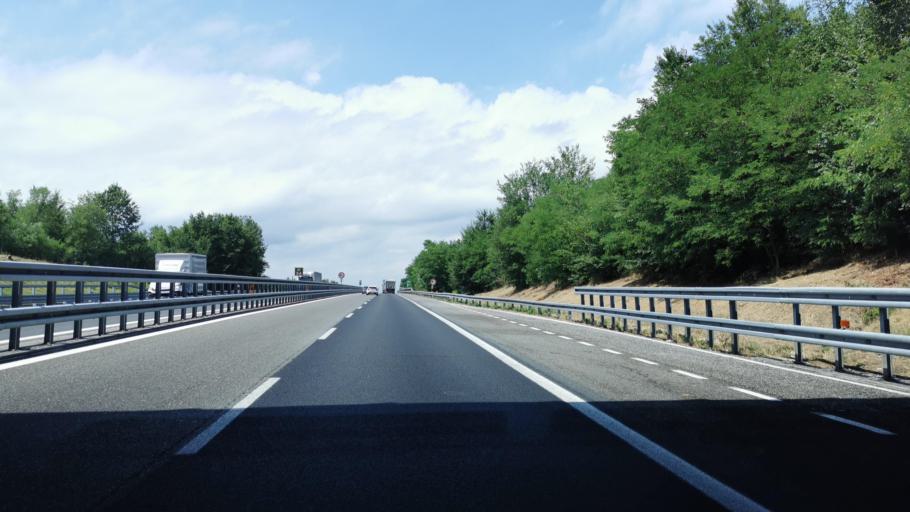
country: IT
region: Piedmont
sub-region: Provincia di Alessandria
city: Quattordio
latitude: 44.9066
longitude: 8.3894
